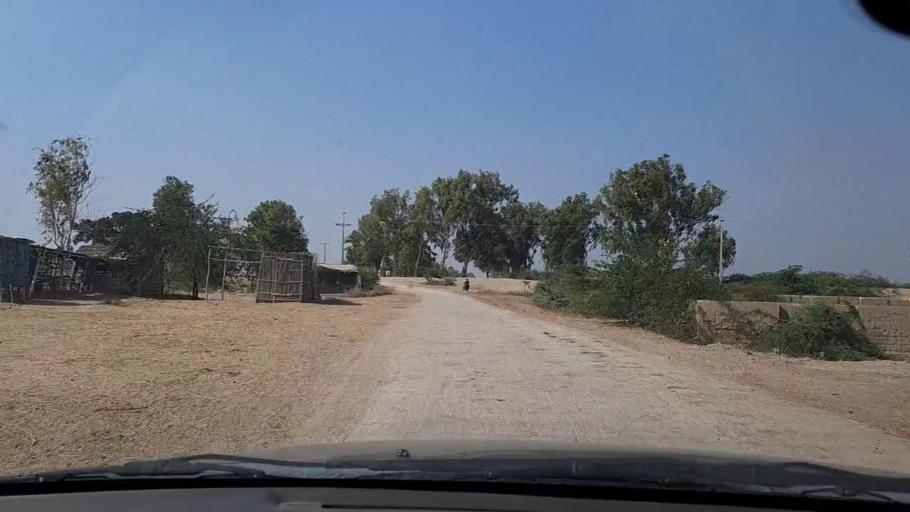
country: PK
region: Sindh
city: Chuhar Jamali
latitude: 24.4237
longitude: 67.8188
